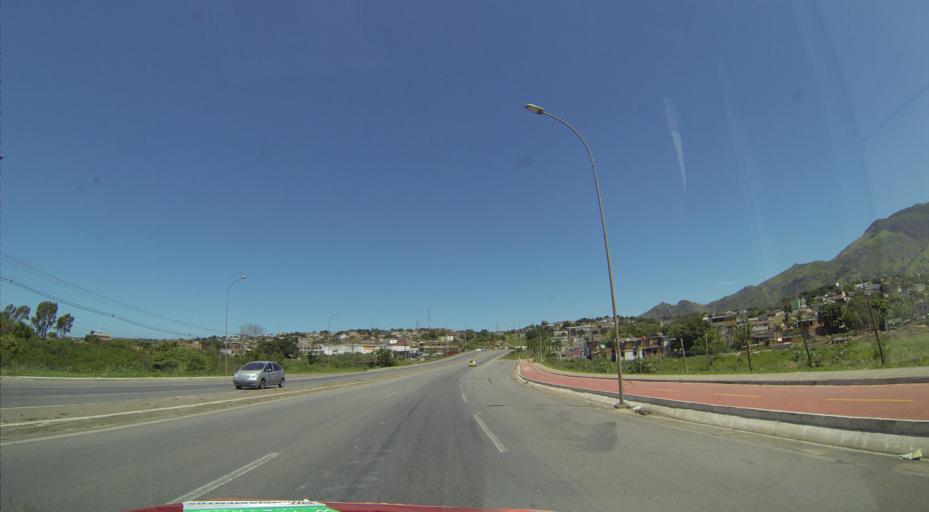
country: BR
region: Espirito Santo
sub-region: Serra
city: Serra
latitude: -20.1329
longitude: -40.2937
